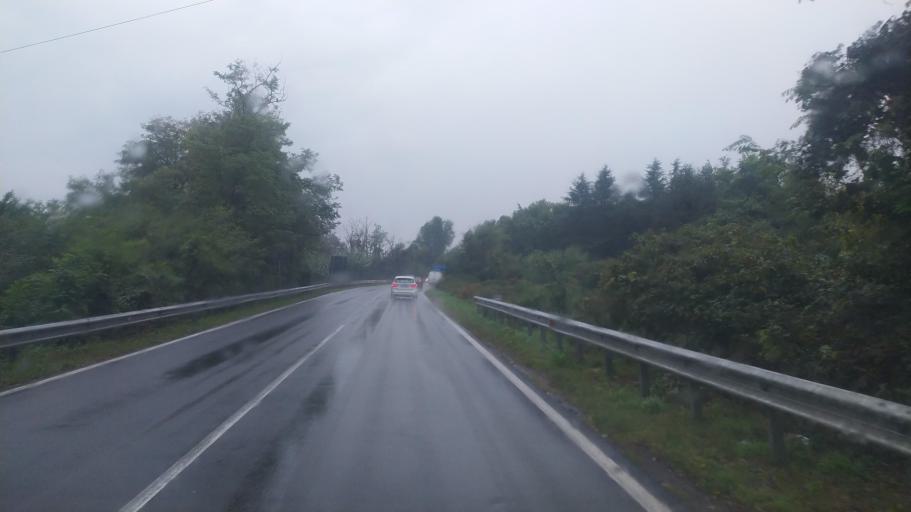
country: IT
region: Lombardy
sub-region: Citta metropolitana di Milano
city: Cusago
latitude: 45.4500
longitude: 9.0468
